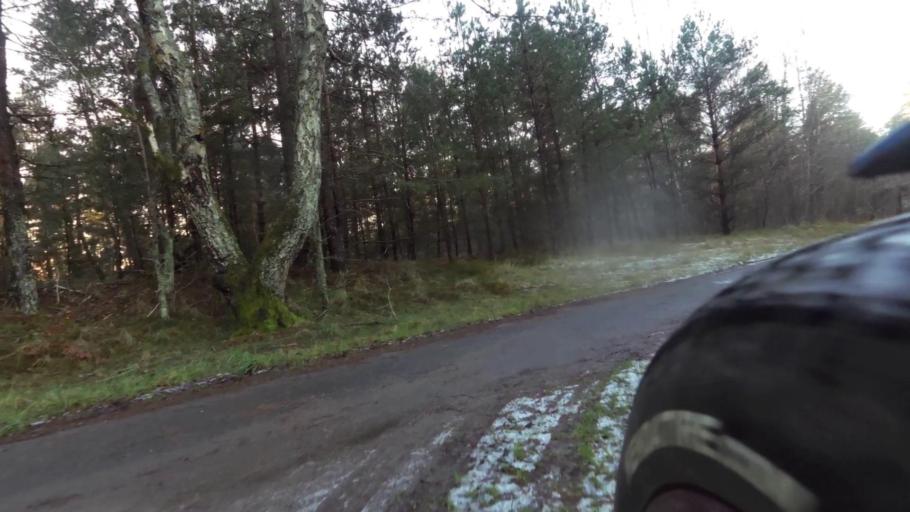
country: PL
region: West Pomeranian Voivodeship
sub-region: Powiat szczecinecki
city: Borne Sulinowo
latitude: 53.5926
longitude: 16.5183
